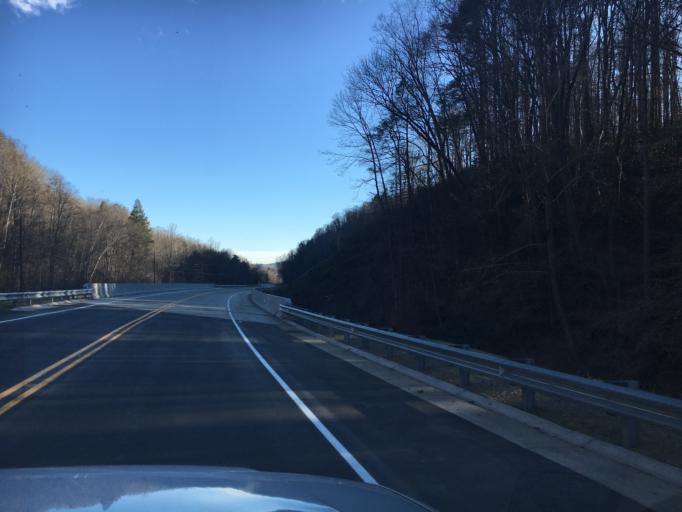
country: US
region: North Carolina
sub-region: McDowell County
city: West Marion
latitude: 35.5762
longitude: -81.9767
